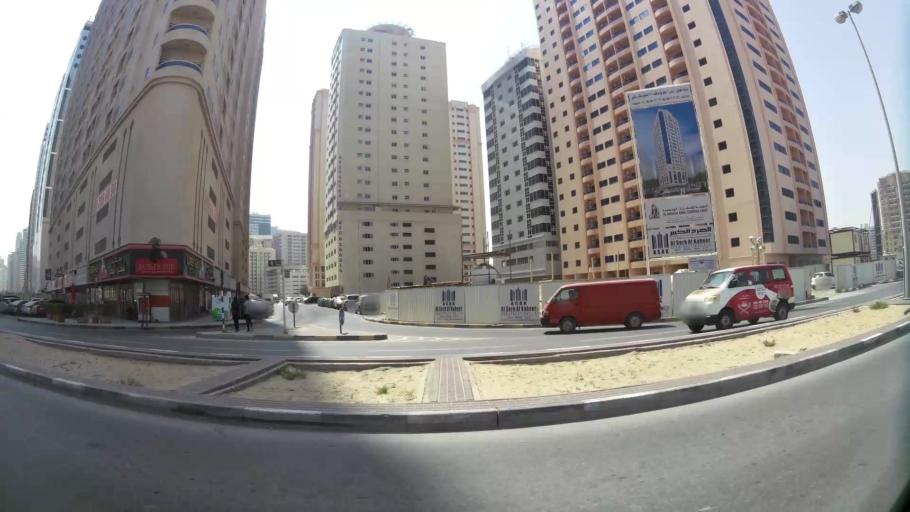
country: AE
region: Ash Shariqah
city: Sharjah
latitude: 25.2996
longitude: 55.3695
